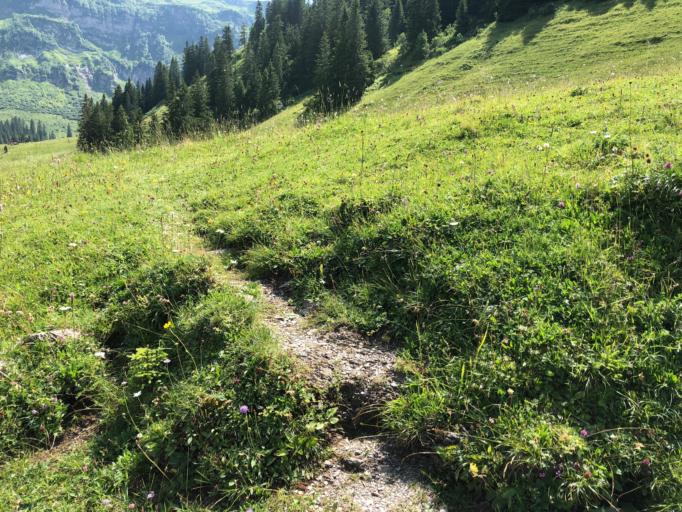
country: AT
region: Vorarlberg
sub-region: Politischer Bezirk Bregenz
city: Reuthe
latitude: 47.3282
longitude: 9.8968
